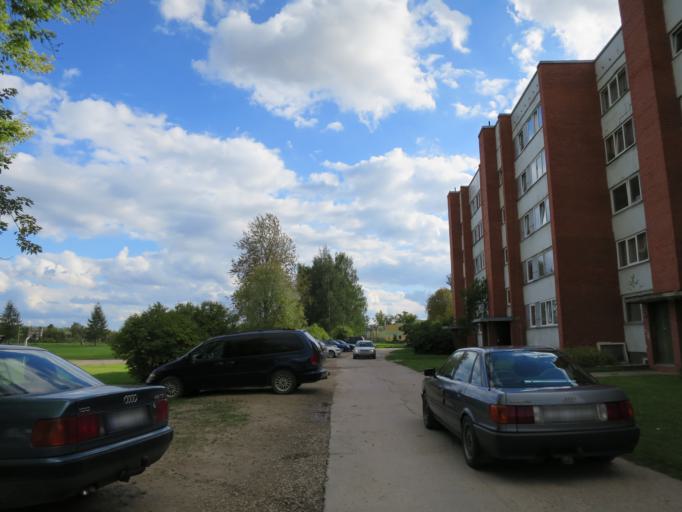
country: LV
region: Sigulda
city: Sigulda
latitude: 57.1497
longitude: 24.8957
